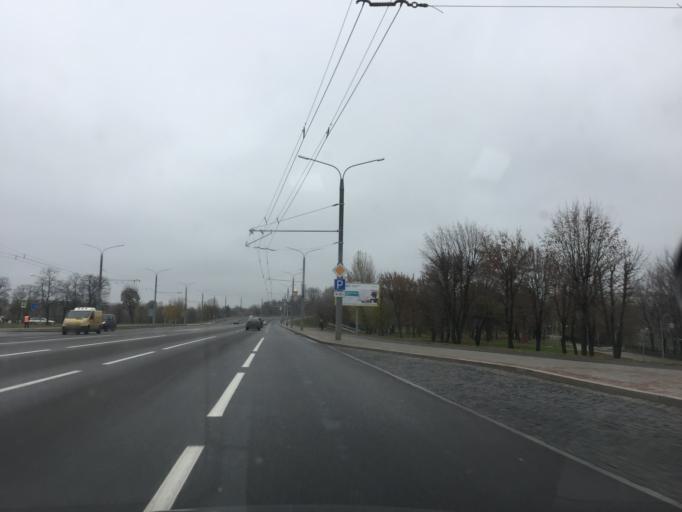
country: BY
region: Mogilev
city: Mahilyow
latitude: 53.8871
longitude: 30.3315
